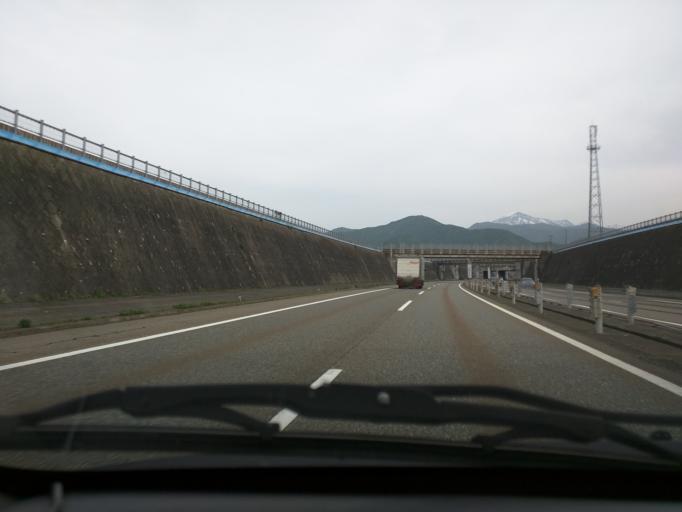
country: JP
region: Niigata
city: Ojiya
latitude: 37.2385
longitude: 138.9711
